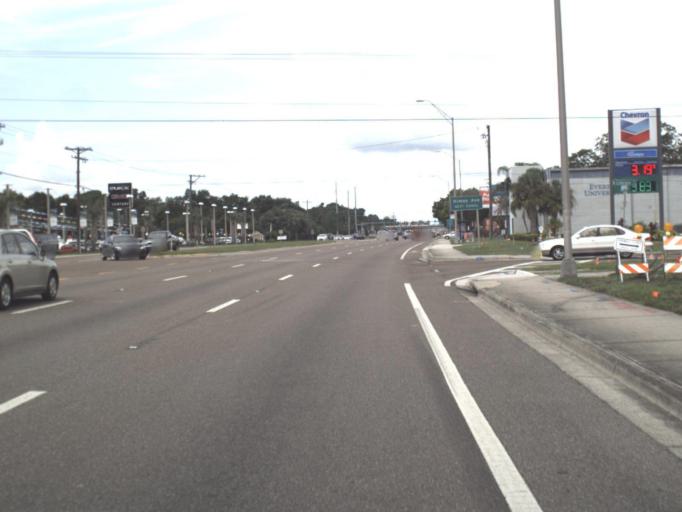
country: US
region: Florida
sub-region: Hillsborough County
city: Egypt Lake-Leto
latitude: 27.9962
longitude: -82.4964
